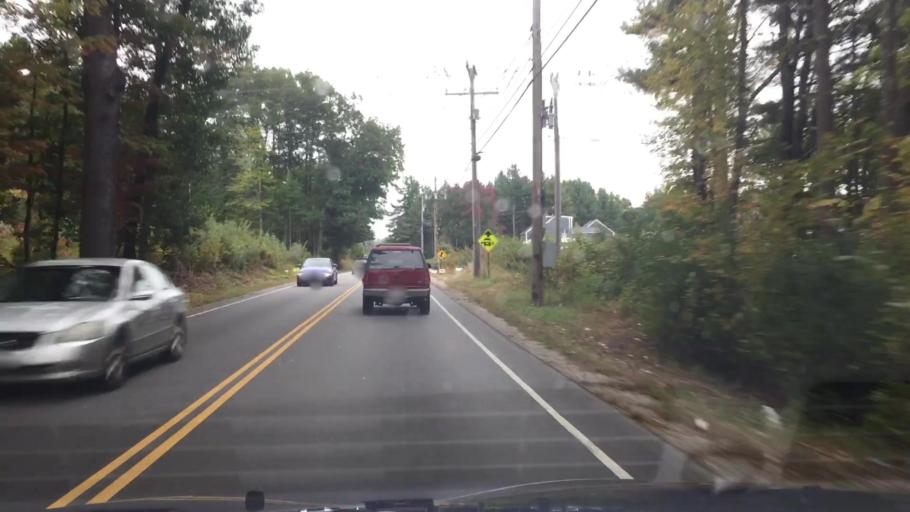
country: US
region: Massachusetts
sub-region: Middlesex County
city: Tyngsboro
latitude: 42.7161
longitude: -71.4146
